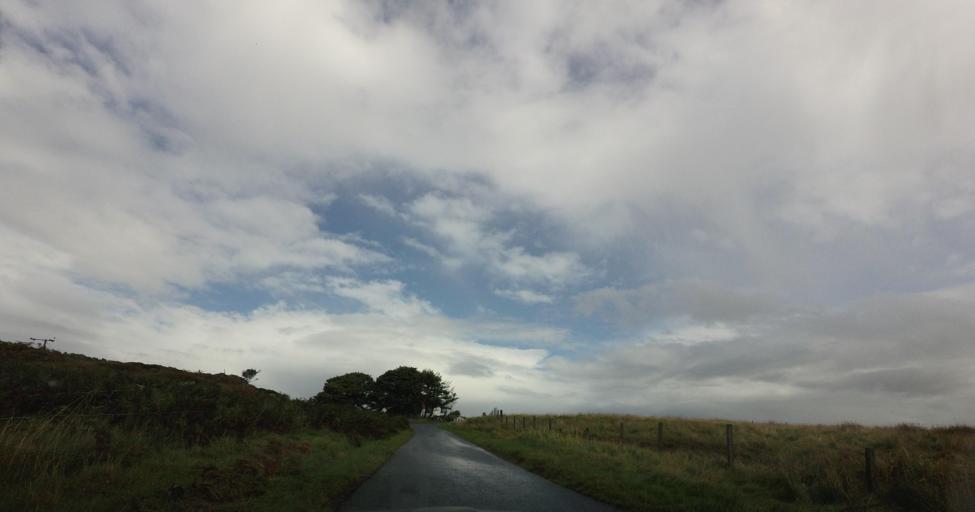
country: GB
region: Scotland
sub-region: Highland
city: Isle of Skye
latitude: 57.1408
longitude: -6.0731
